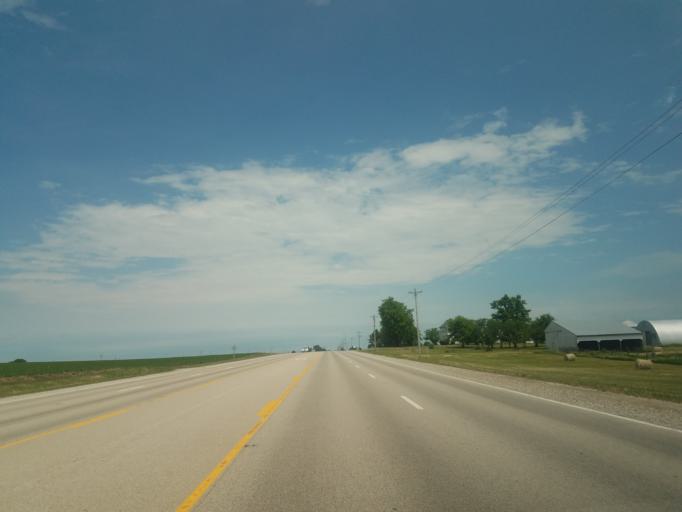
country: US
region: Illinois
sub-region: McLean County
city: Downs
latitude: 40.4271
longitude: -88.9011
